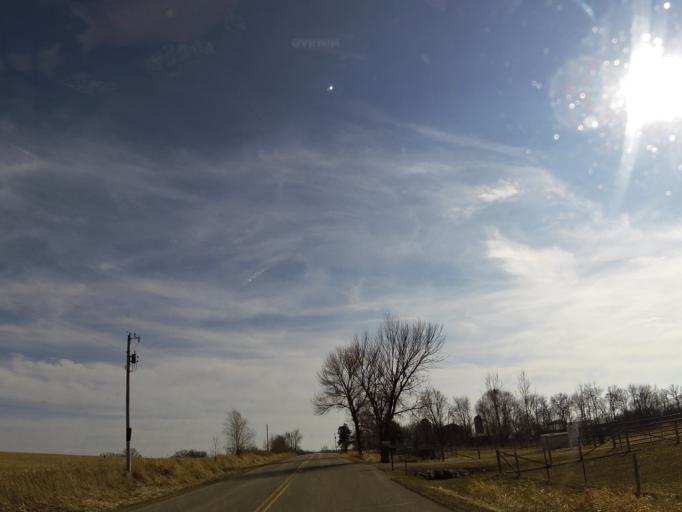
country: US
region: Minnesota
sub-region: Scott County
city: Prior Lake
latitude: 44.6732
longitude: -93.4808
